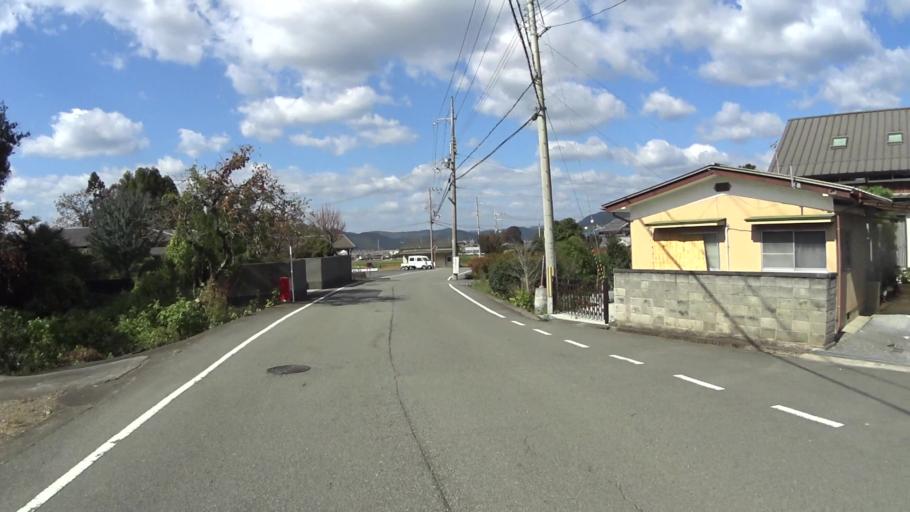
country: JP
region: Kyoto
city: Kameoka
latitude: 35.0872
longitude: 135.5615
